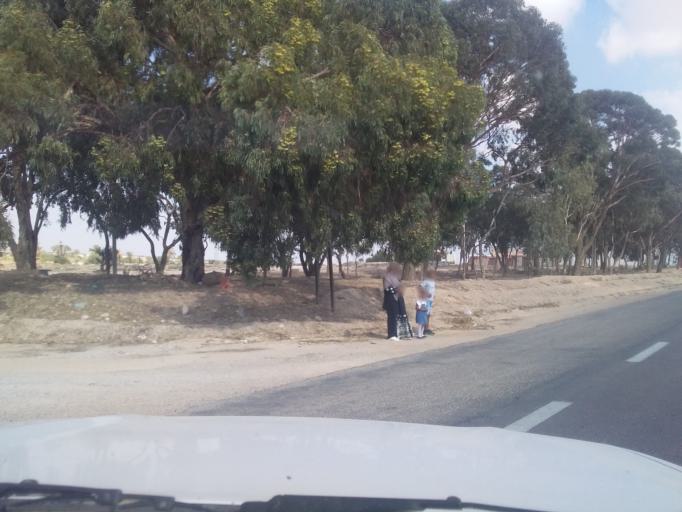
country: TN
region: Qabis
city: Gabes
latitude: 33.6315
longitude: 10.2818
